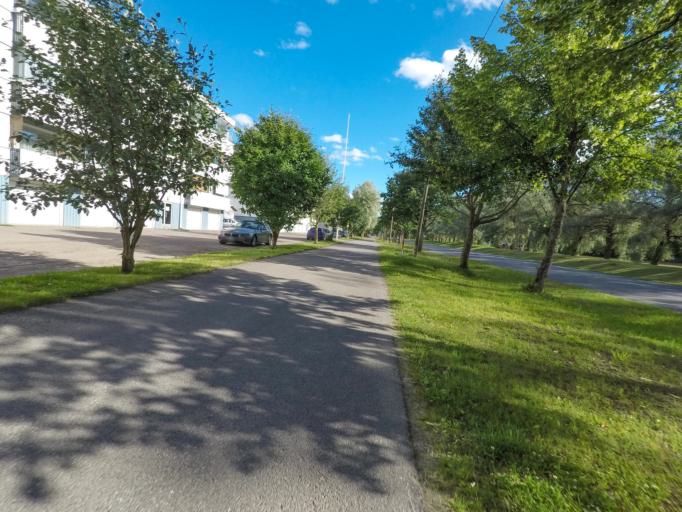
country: FI
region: South Karelia
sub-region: Lappeenranta
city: Lappeenranta
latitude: 61.0799
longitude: 28.1495
